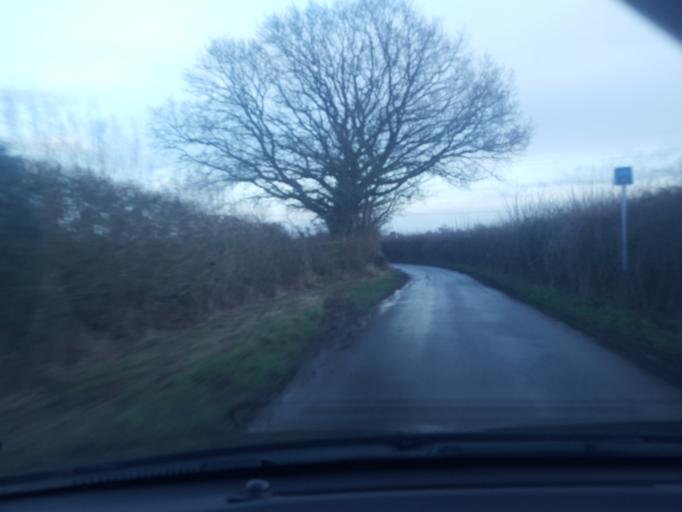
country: GB
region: England
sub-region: Staffordshire
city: Codsall
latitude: 52.6334
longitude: -2.2216
